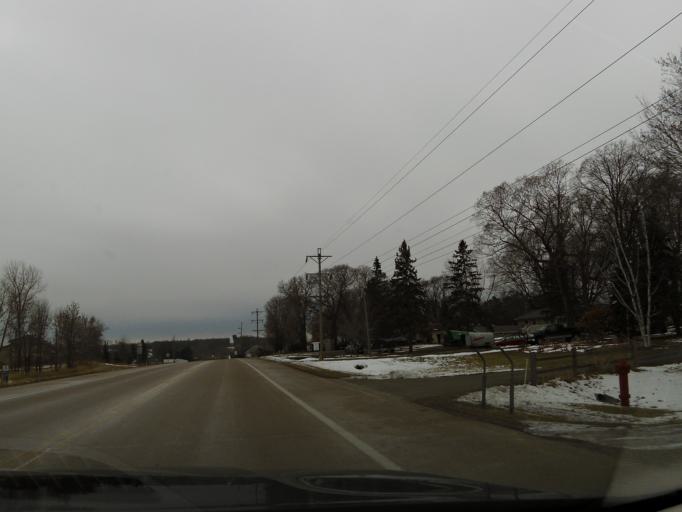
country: US
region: Minnesota
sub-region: Carver County
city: Watertown
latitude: 44.9535
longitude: -93.8386
